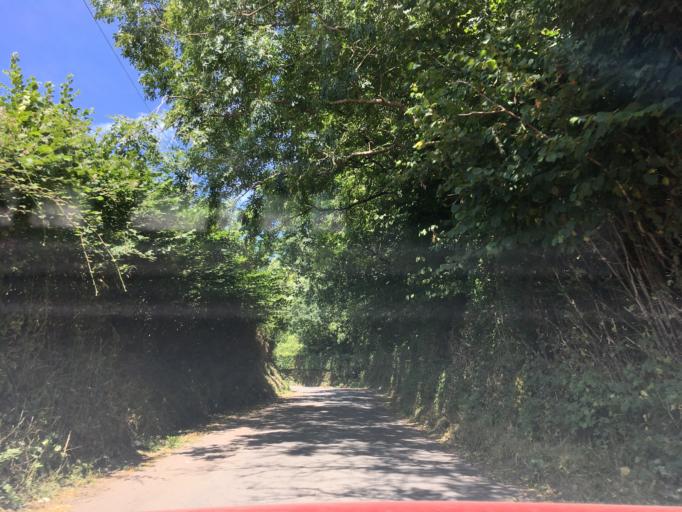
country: GB
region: Wales
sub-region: Caerphilly County Borough
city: Machen
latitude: 51.5483
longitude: -3.1410
